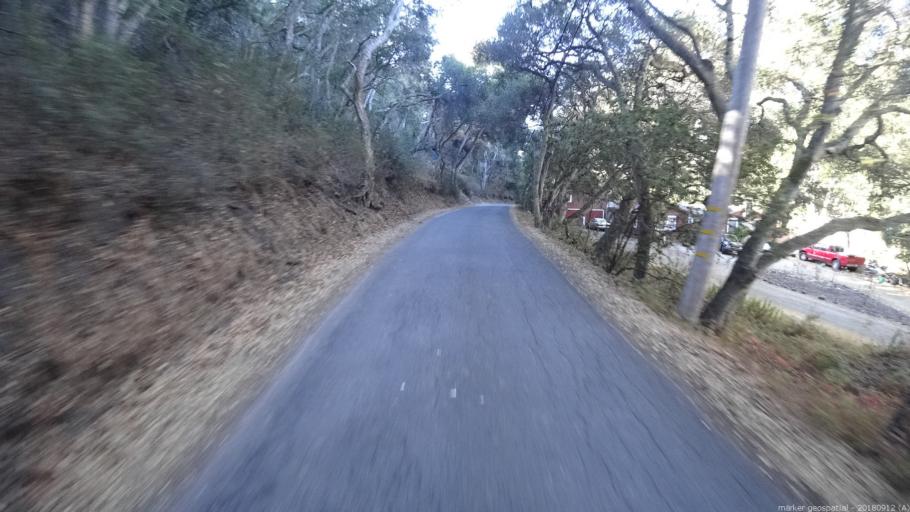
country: US
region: California
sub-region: Monterey County
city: Carmel Valley Village
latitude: 36.5432
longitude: -121.7353
